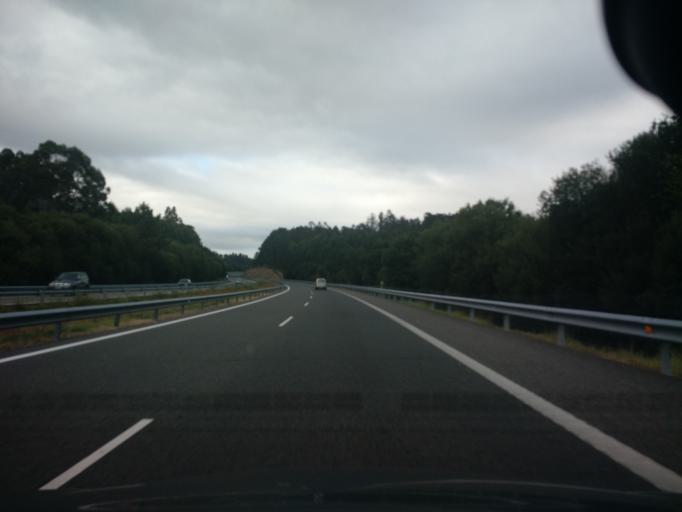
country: ES
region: Galicia
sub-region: Provincia da Coruna
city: Abegondo
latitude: 43.2232
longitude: -8.2747
